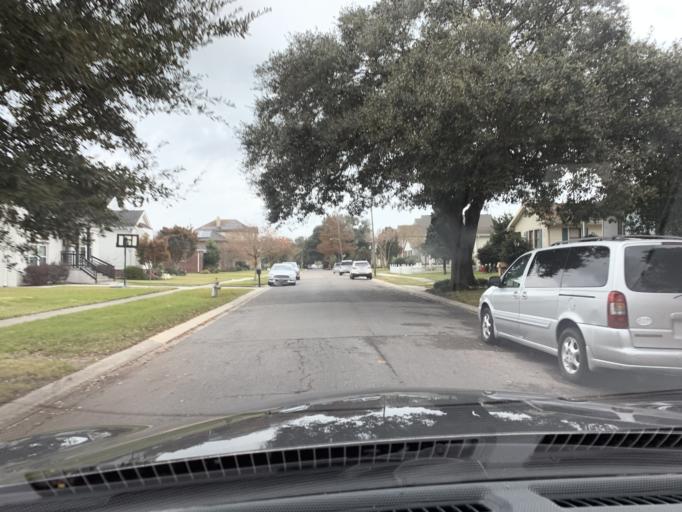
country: US
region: Louisiana
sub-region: Jefferson Parish
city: Metairie
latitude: 30.0069
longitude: -90.1012
